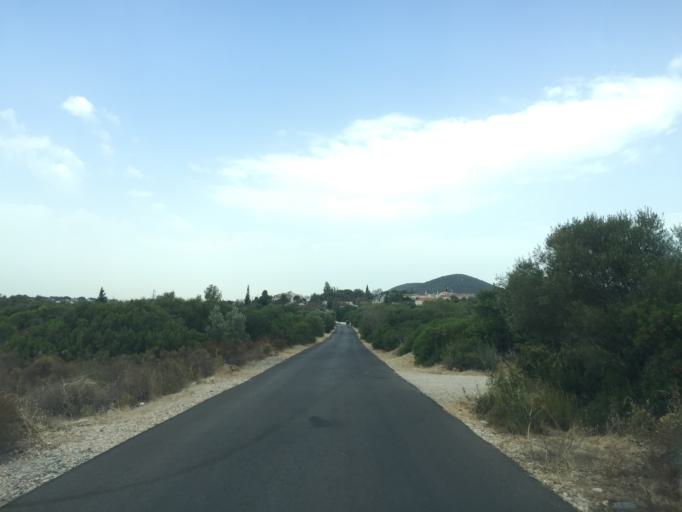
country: PT
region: Faro
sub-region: Loule
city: Almancil
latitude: 37.0988
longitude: -8.0353
